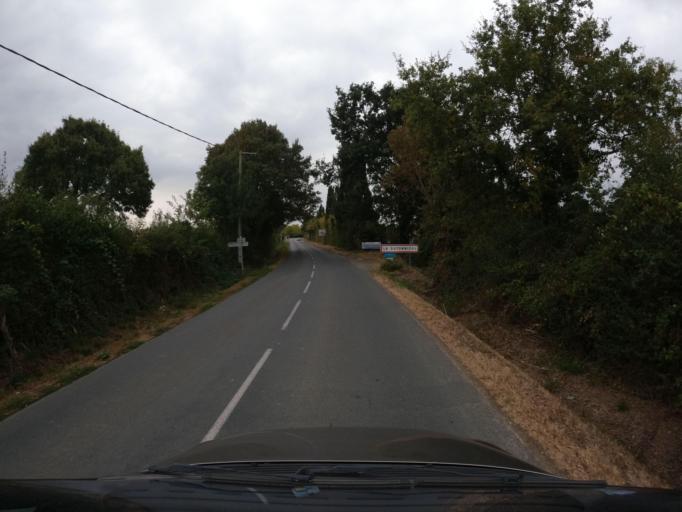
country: FR
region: Pays de la Loire
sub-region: Departement de la Vendee
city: La Guyonniere
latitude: 46.9701
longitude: -1.2462
